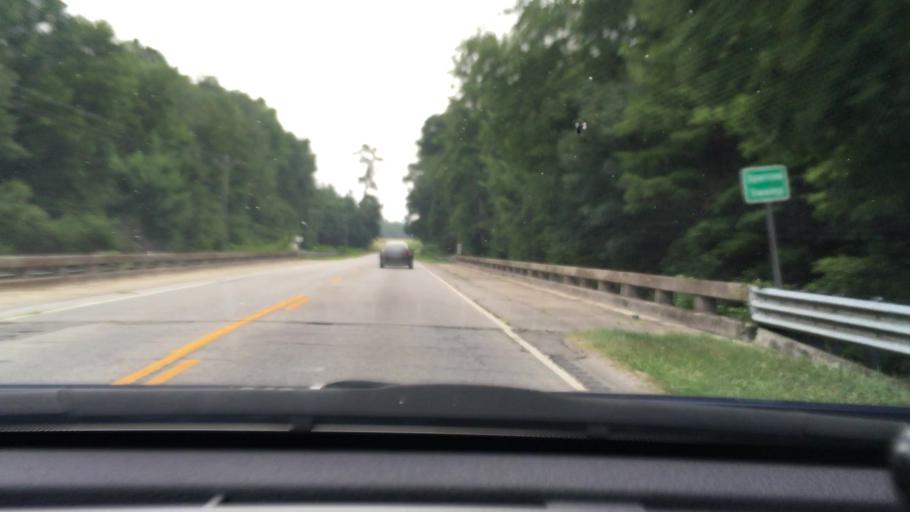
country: US
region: South Carolina
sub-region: Florence County
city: Timmonsville
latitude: 34.1921
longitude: -80.0420
